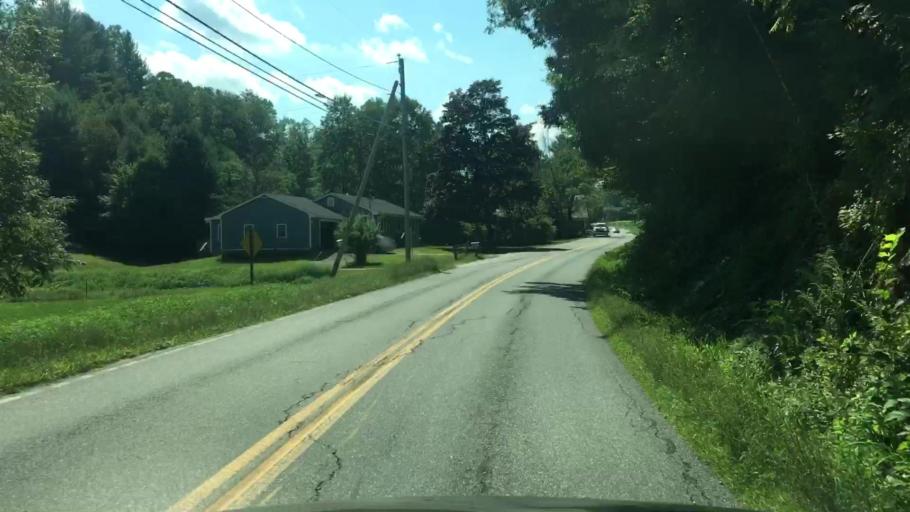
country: US
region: Vermont
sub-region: Windham County
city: West Brattleboro
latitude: 42.7888
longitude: -72.5991
